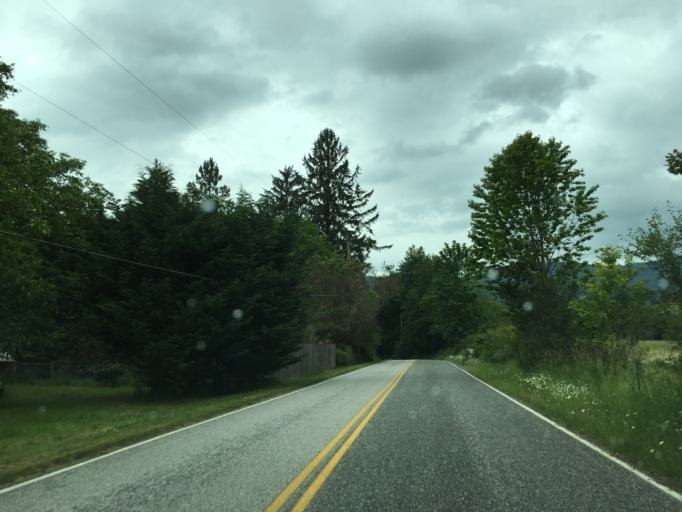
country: US
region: Washington
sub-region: Whatcom County
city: Peaceful Valley
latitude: 48.9979
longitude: -122.0685
